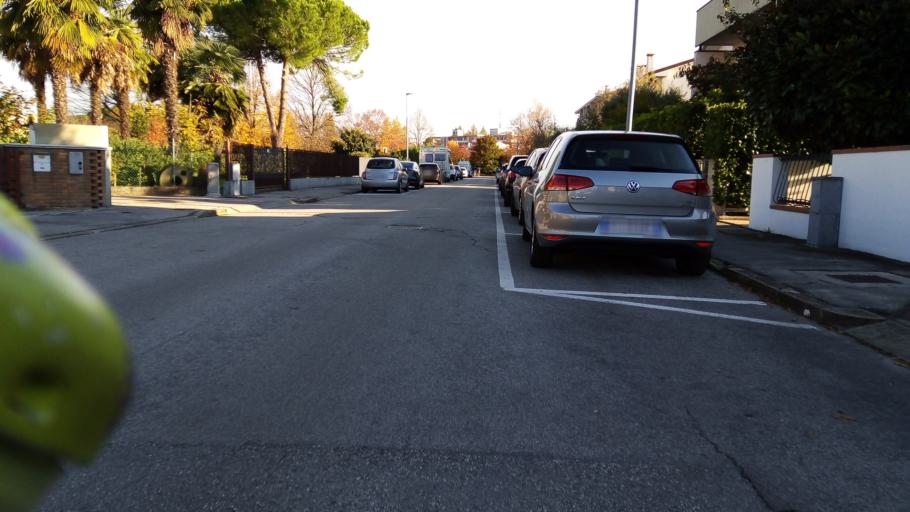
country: IT
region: Veneto
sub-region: Provincia di Padova
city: Abano Terme
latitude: 45.3590
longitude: 11.7803
